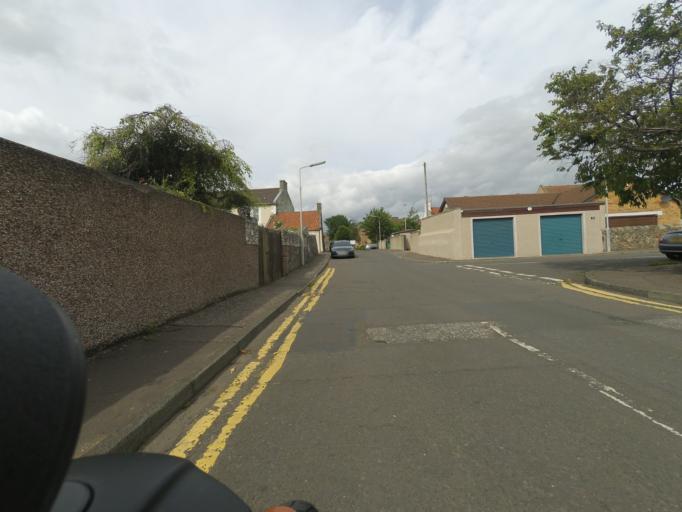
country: GB
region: Scotland
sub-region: Fife
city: Leven
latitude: 56.1931
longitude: -2.9966
